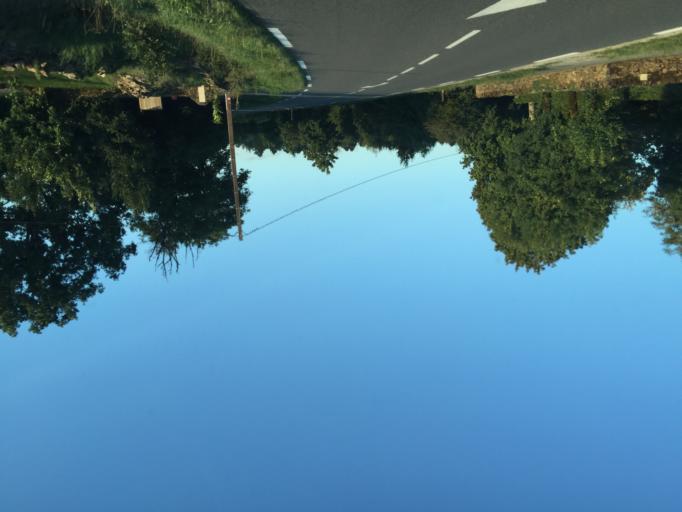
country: FR
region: Midi-Pyrenees
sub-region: Departement de l'Aveyron
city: Sebazac-Concoures
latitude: 44.3976
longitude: 2.5623
